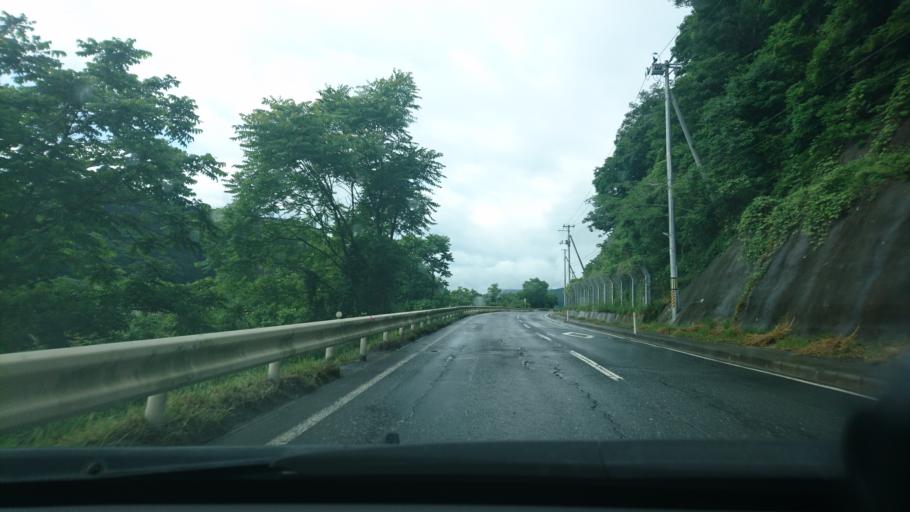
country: JP
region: Miyagi
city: Ishinomaki
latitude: 38.5781
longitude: 141.3018
